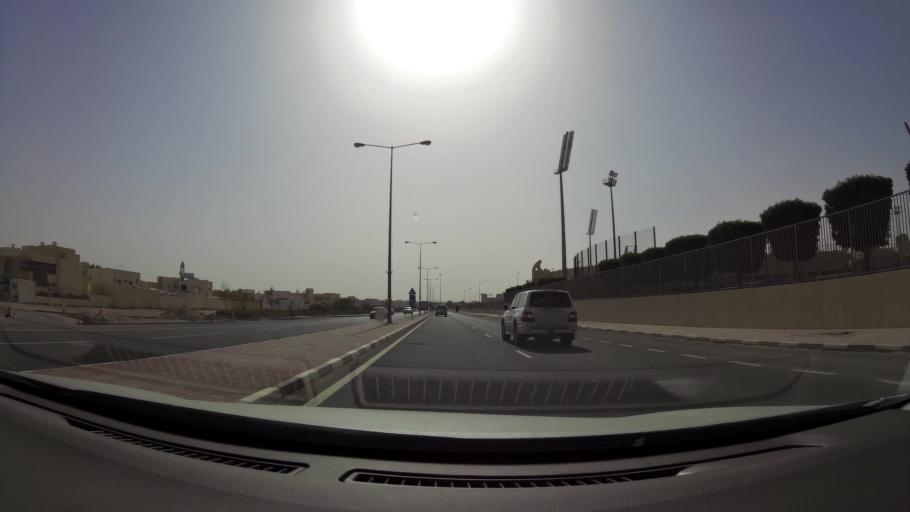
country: QA
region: Baladiyat ar Rayyan
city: Ar Rayyan
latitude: 25.3442
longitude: 51.4429
